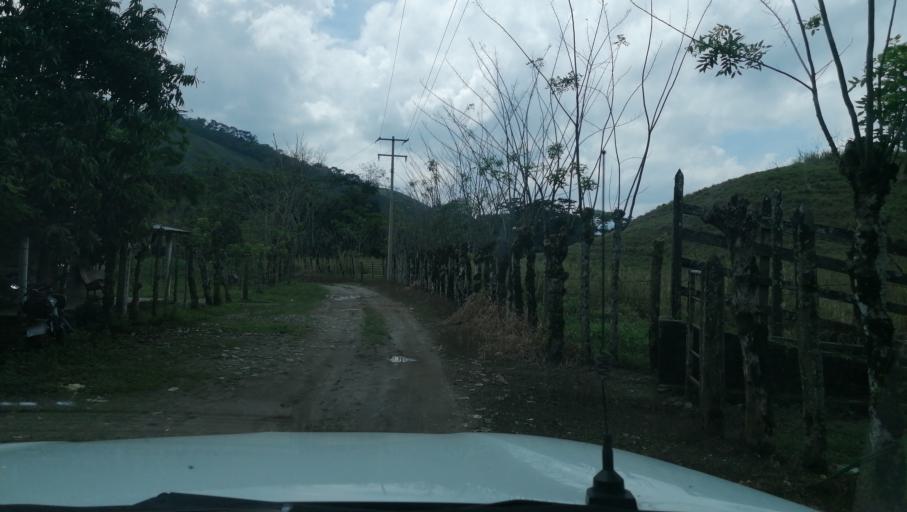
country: MX
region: Chiapas
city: Pichucalco
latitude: 17.4563
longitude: -93.2039
